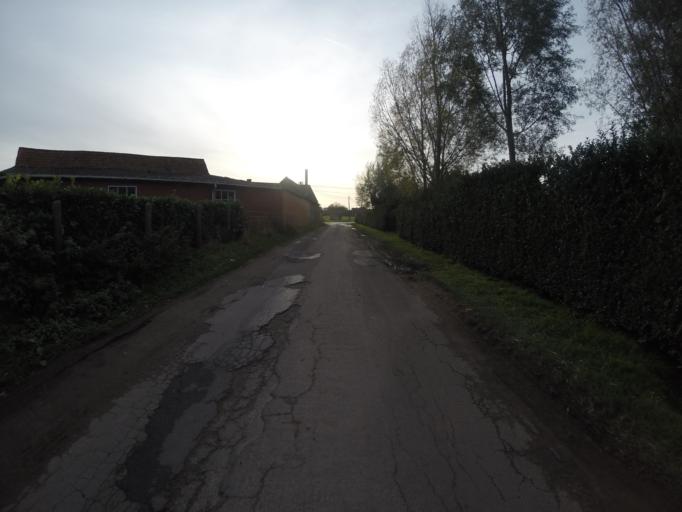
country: BE
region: Flanders
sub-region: Provincie Oost-Vlaanderen
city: Aalter
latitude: 51.0583
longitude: 3.4812
